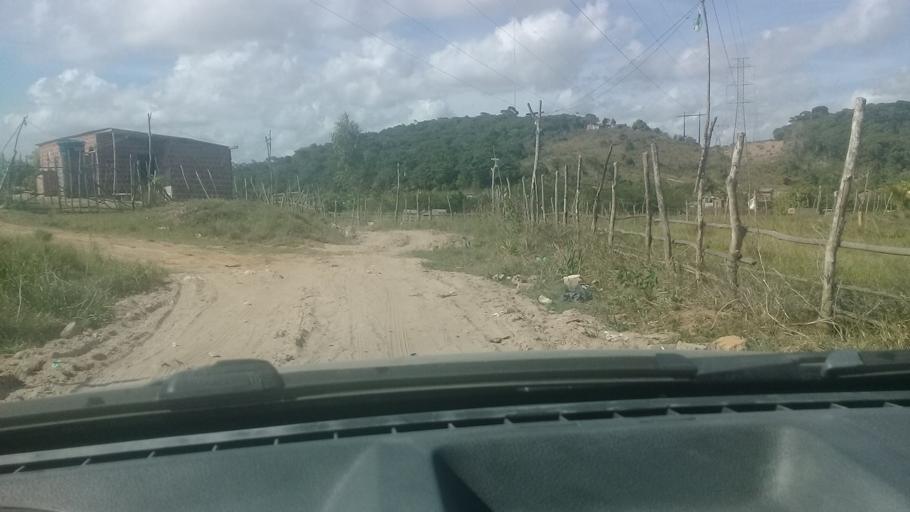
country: BR
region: Pernambuco
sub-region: Jaboatao Dos Guararapes
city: Jaboatao dos Guararapes
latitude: -8.0867
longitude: -35.0338
